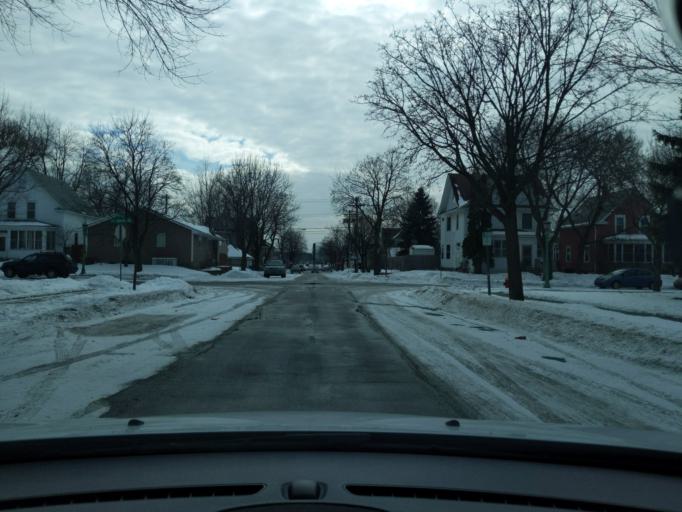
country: US
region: Minnesota
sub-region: Ramsey County
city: Falcon Heights
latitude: 44.9578
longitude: -93.1637
